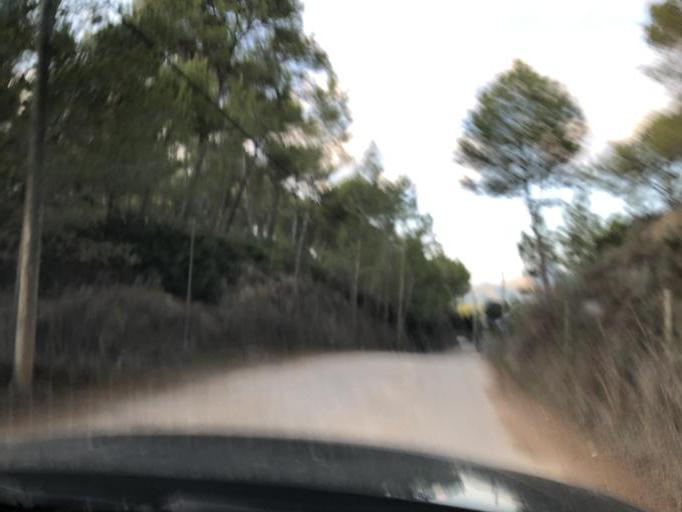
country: ES
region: Balearic Islands
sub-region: Illes Balears
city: Santa Ponsa
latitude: 39.5401
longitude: 2.4837
